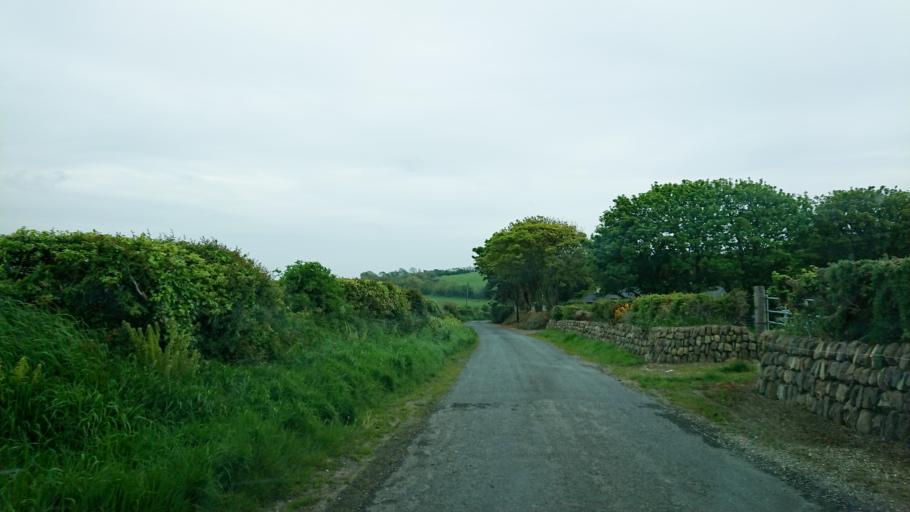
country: IE
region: Munster
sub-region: Waterford
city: Dunmore East
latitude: 52.2228
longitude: -7.0168
